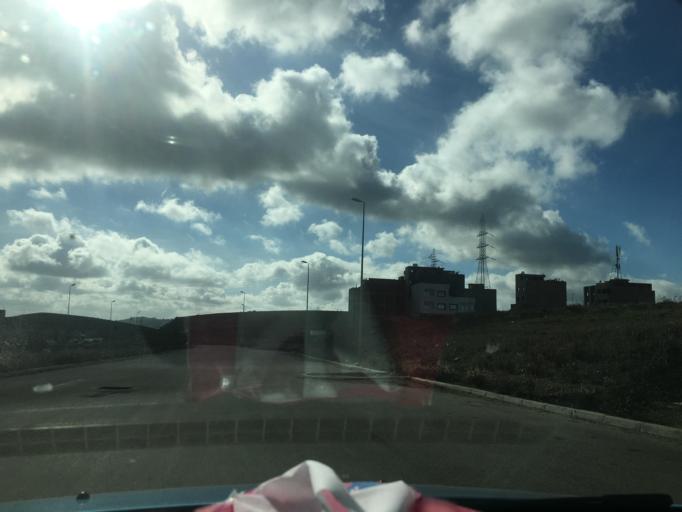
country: MA
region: Tanger-Tetouan
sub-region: Tanger-Assilah
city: Tangier
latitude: 35.7112
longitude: -5.8171
